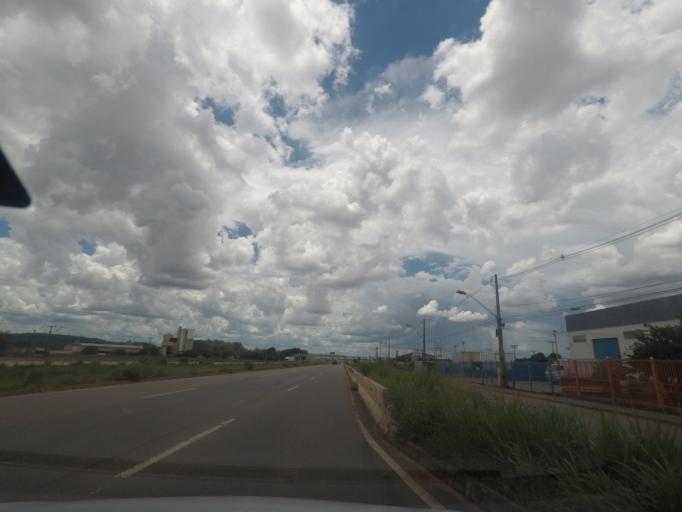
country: BR
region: Goias
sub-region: Goiania
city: Goiania
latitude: -16.7157
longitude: -49.3626
